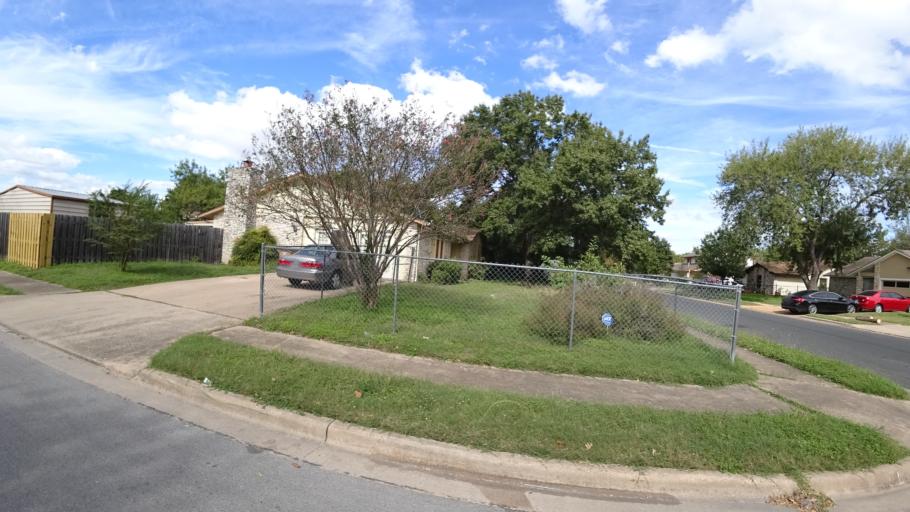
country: US
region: Texas
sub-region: Travis County
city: Austin
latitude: 30.2002
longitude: -97.7412
